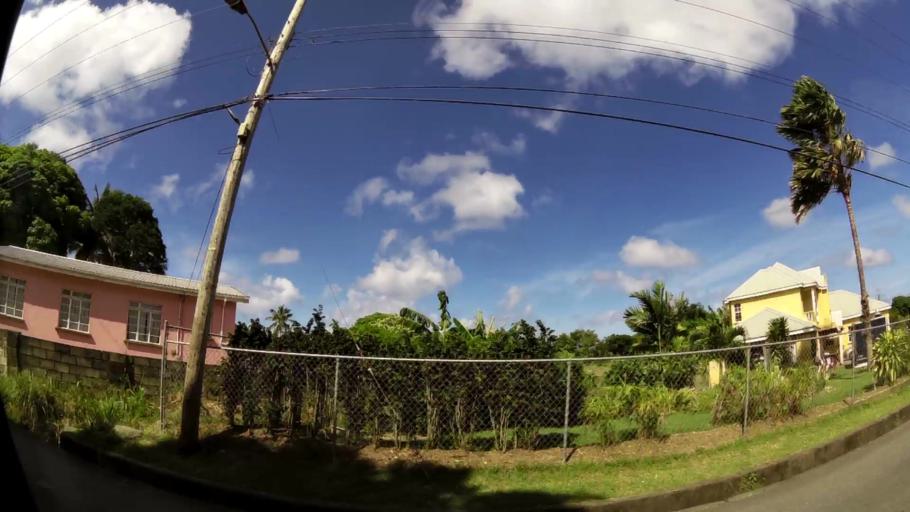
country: BB
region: Saint Peter
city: Speightstown
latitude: 13.2572
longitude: -59.6345
